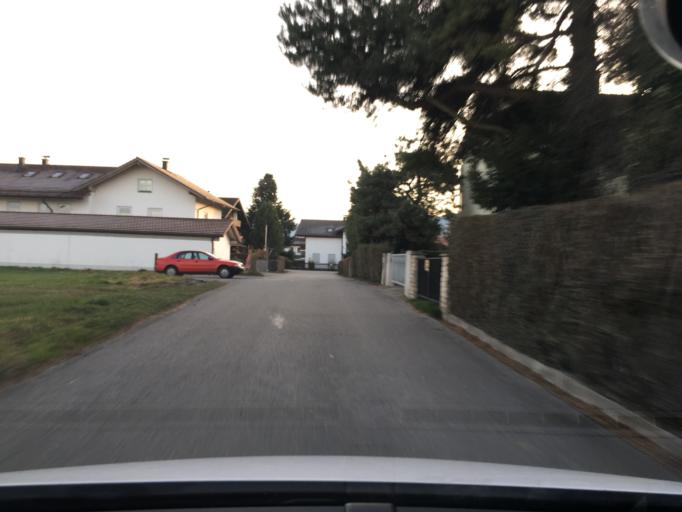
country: DE
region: Bavaria
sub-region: Upper Bavaria
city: Raubling
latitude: 47.7898
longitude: 12.1031
